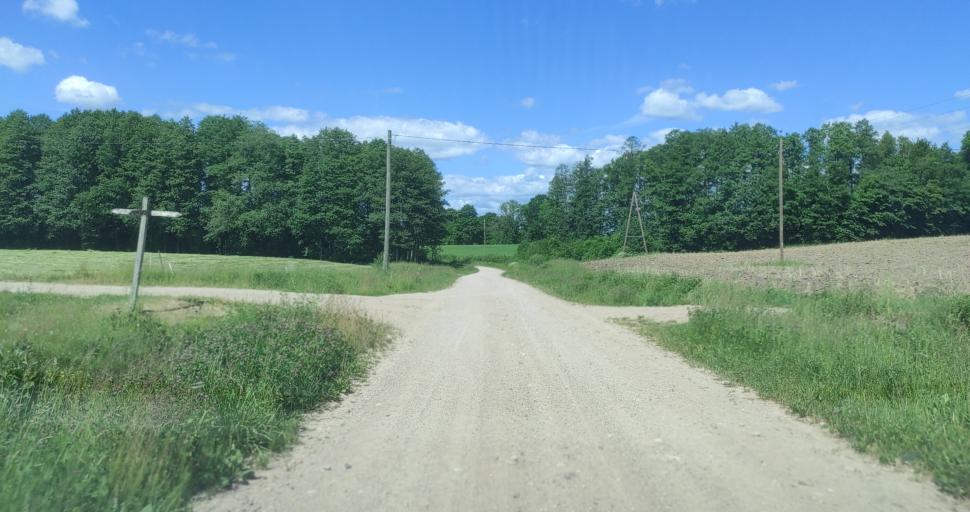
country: LV
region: Alsunga
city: Alsunga
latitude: 56.8713
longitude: 21.7099
